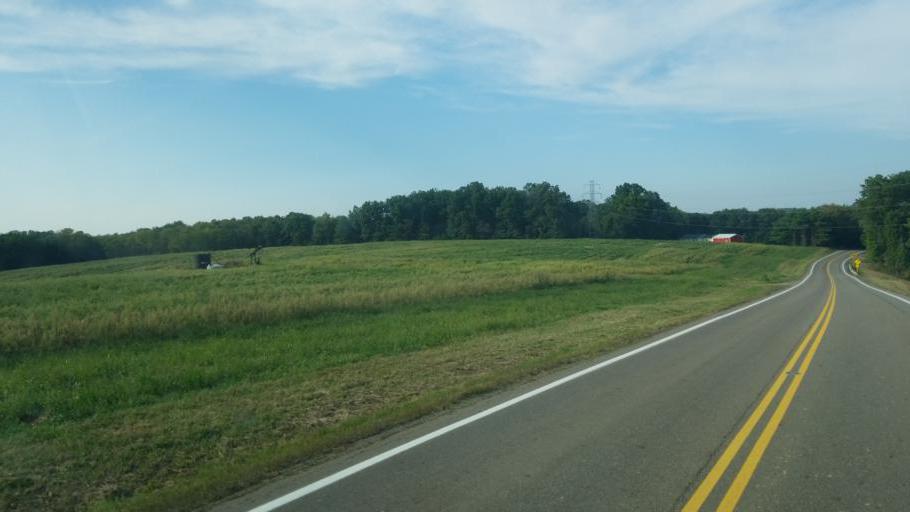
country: US
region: Ohio
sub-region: Knox County
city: Oak Hill
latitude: 40.3841
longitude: -82.2808
